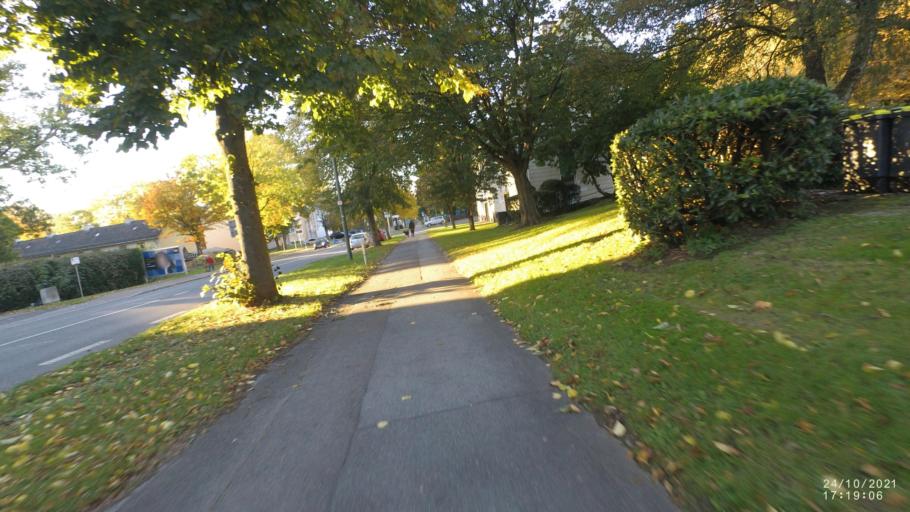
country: DE
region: North Rhine-Westphalia
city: Iserlohn
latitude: 51.3749
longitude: 7.7337
